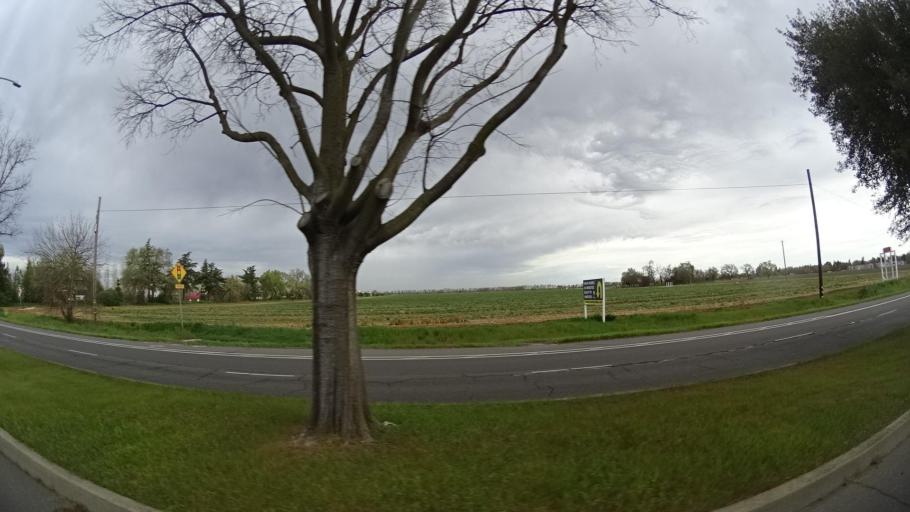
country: US
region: California
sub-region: Yolo County
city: Davis
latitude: 38.5604
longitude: -121.7365
